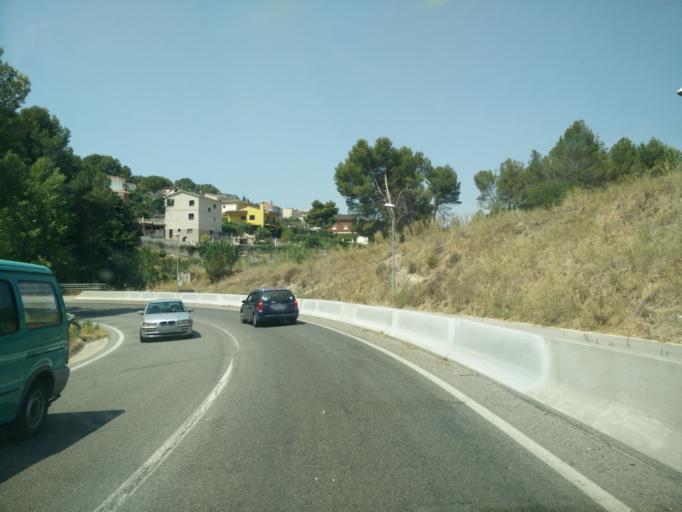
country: ES
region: Catalonia
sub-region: Provincia de Barcelona
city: Esparreguera
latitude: 41.5299
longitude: 1.8589
